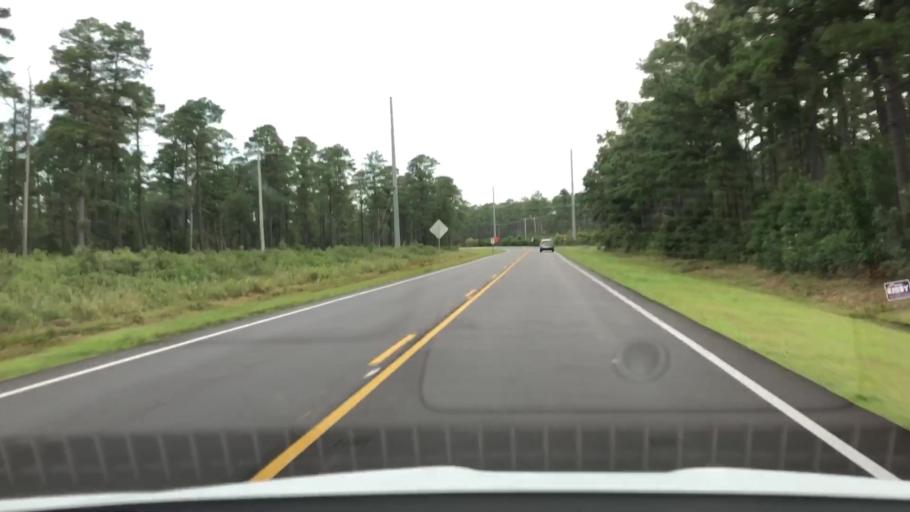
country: US
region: North Carolina
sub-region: Onslow County
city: Swansboro
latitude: 34.8063
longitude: -77.1337
